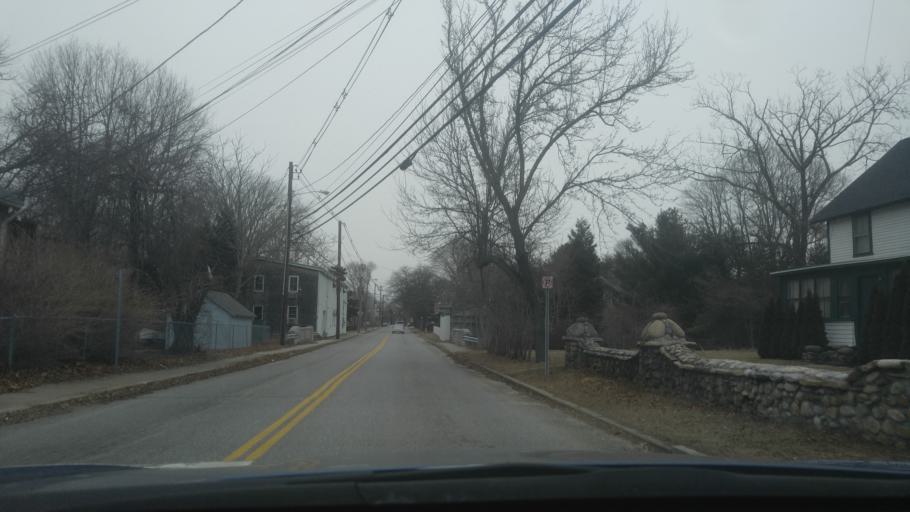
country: US
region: Rhode Island
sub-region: Washington County
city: Wakefield-Peacedale
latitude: 41.4385
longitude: -71.4951
